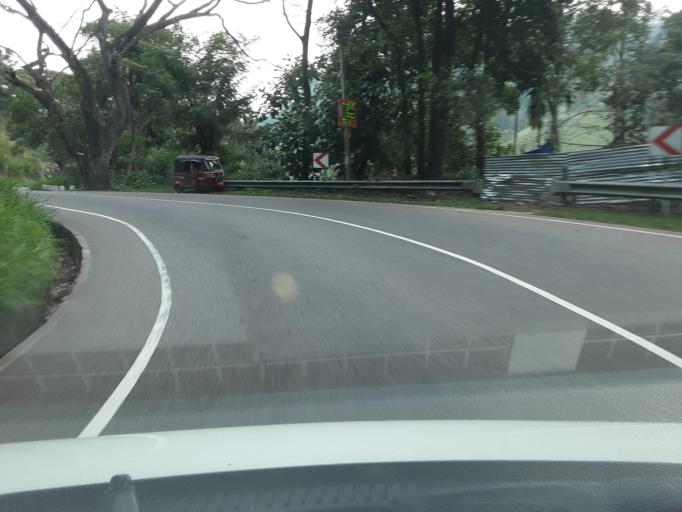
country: LK
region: Uva
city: Badulla
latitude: 6.9410
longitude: 81.0168
